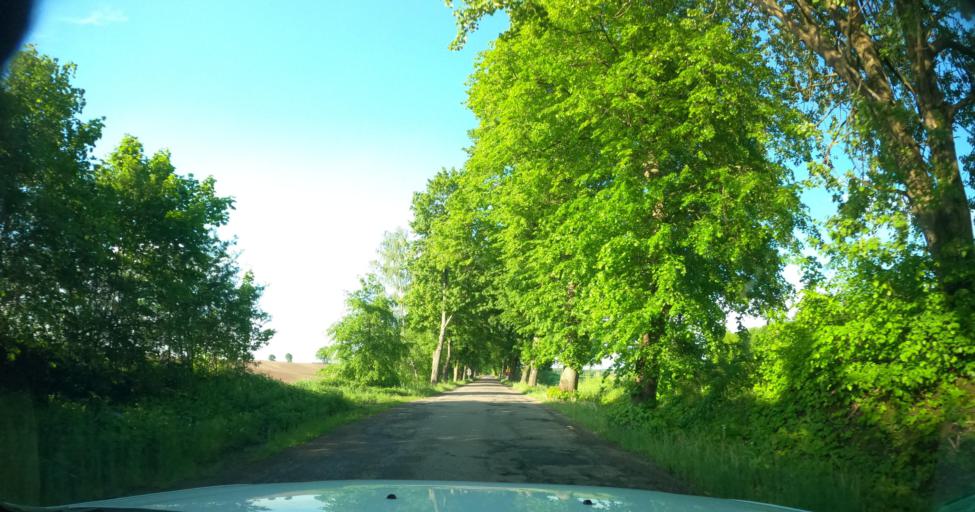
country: PL
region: Warmian-Masurian Voivodeship
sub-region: Powiat braniewski
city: Braniewo
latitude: 54.2716
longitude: 19.8323
